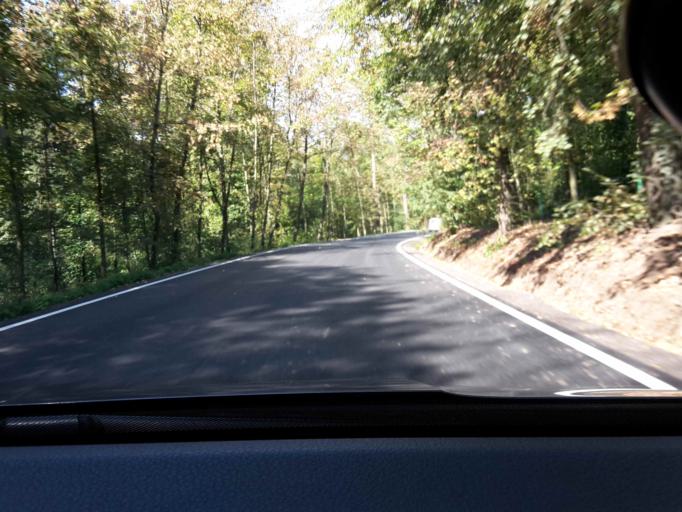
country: CZ
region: Vysocina
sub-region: Okres Jihlava
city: Telc
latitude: 49.1773
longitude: 15.4651
